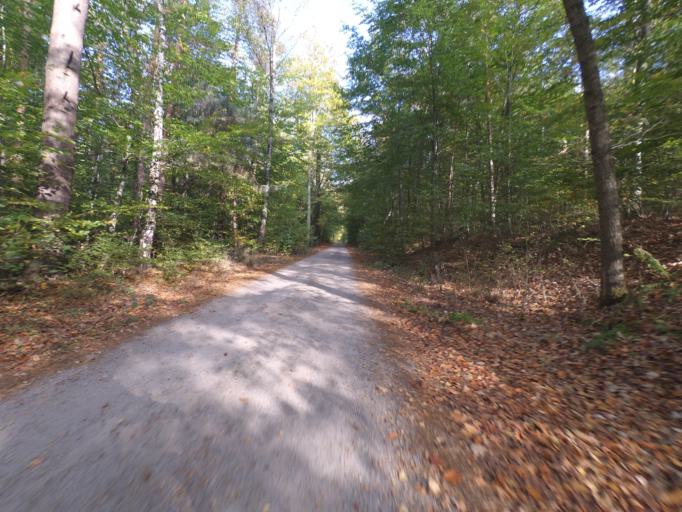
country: DE
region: Saxony
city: Albertstadt
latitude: 51.0947
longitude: 13.7983
